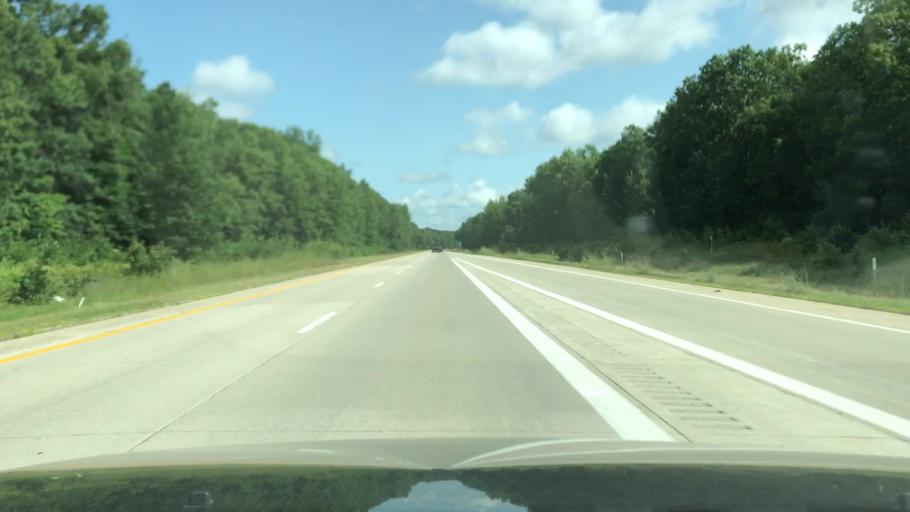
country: US
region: Michigan
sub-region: Montcalm County
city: Howard City
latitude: 43.4000
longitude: -85.5117
